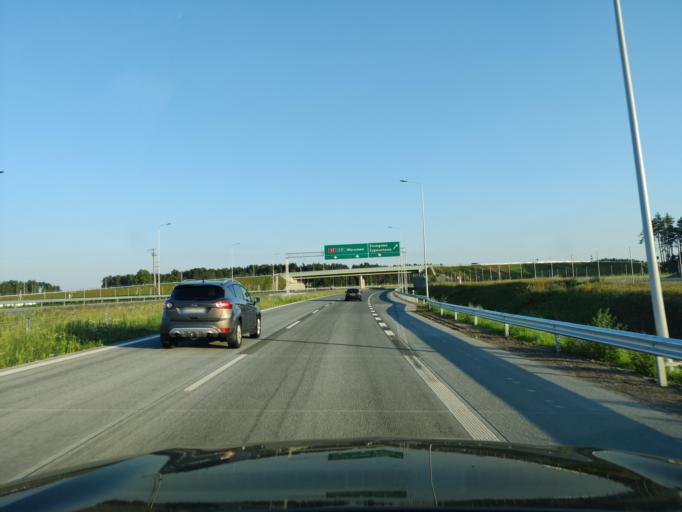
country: PL
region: Masovian Voivodeship
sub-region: Powiat mlawski
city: Strzegowo
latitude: 52.8619
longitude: 20.2870
